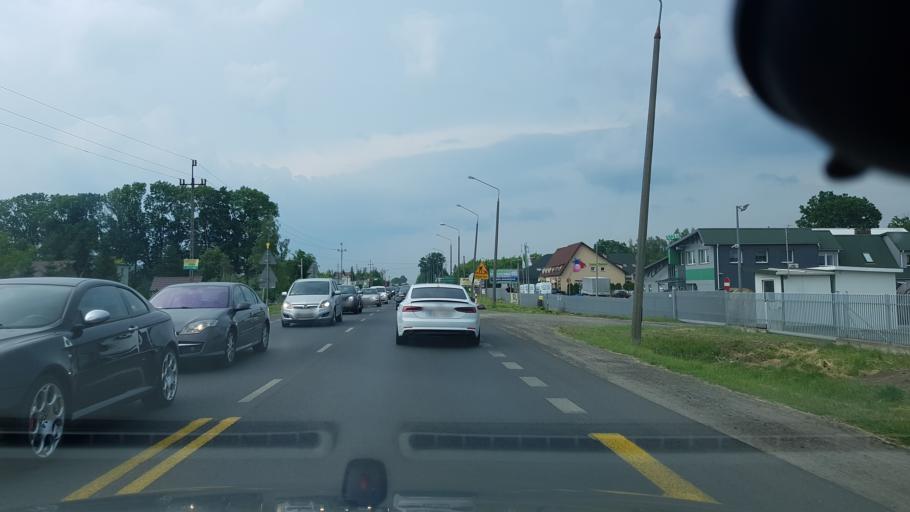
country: PL
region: Masovian Voivodeship
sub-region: Powiat legionowski
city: Michalow-Reginow
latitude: 52.4125
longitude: 20.9603
